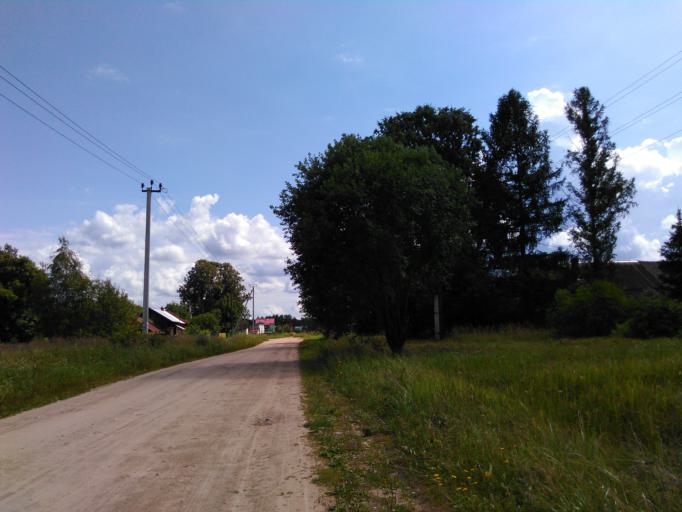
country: RU
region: Vladimir
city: Krasnyy Oktyabr'
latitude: 55.9976
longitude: 38.8550
